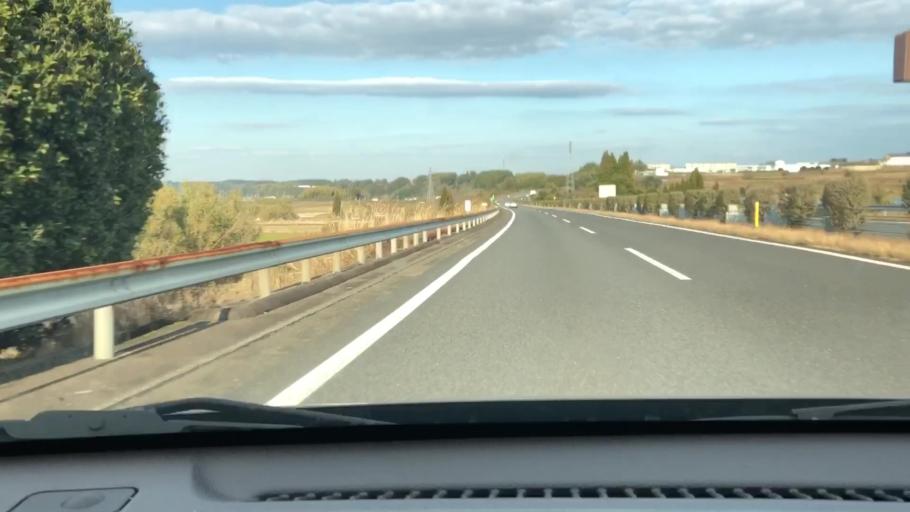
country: JP
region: Miyazaki
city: Miyazaki-shi
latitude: 31.8243
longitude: 131.3075
